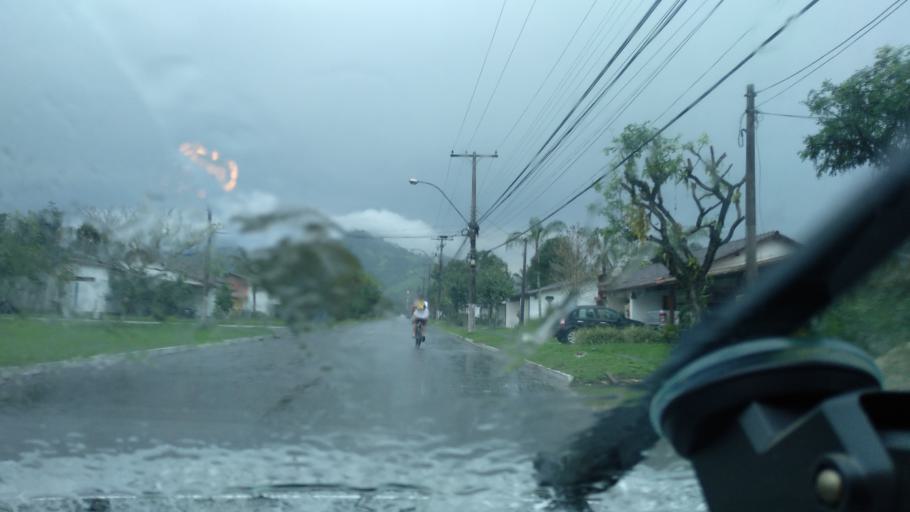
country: BR
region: Rio de Janeiro
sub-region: Angra Dos Reis
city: Angra dos Reis
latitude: -23.0276
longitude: -44.5378
